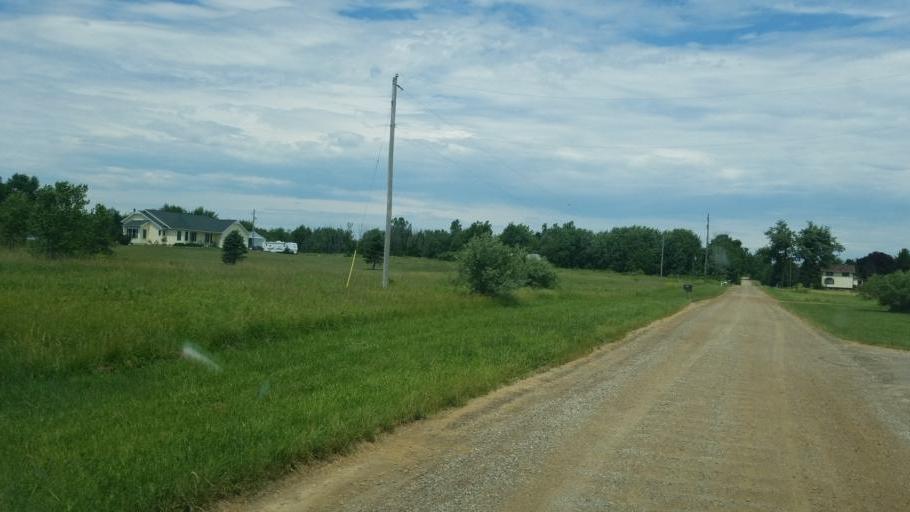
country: US
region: Michigan
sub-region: Eaton County
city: Charlotte
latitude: 42.6463
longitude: -84.9152
